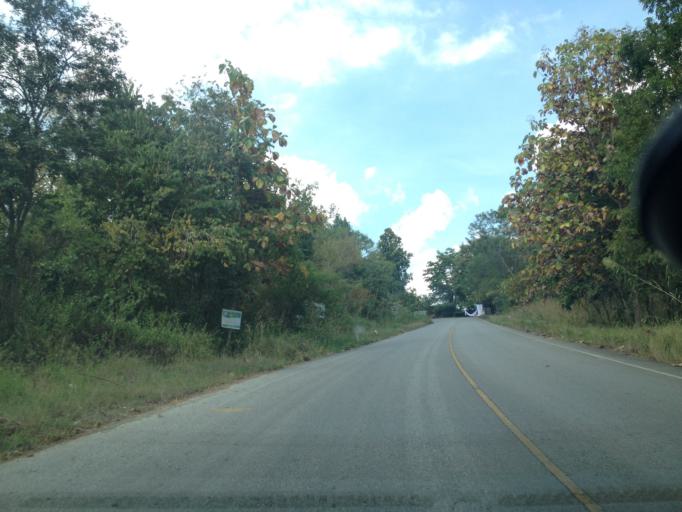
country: TH
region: Chiang Mai
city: Hang Dong
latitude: 18.7742
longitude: 98.8601
